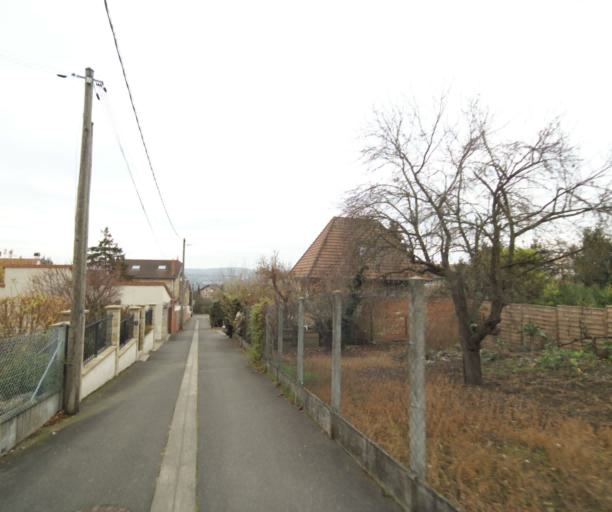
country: FR
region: Ile-de-France
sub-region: Departement des Yvelines
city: Triel-sur-Seine
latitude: 48.9802
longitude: 2.0101
